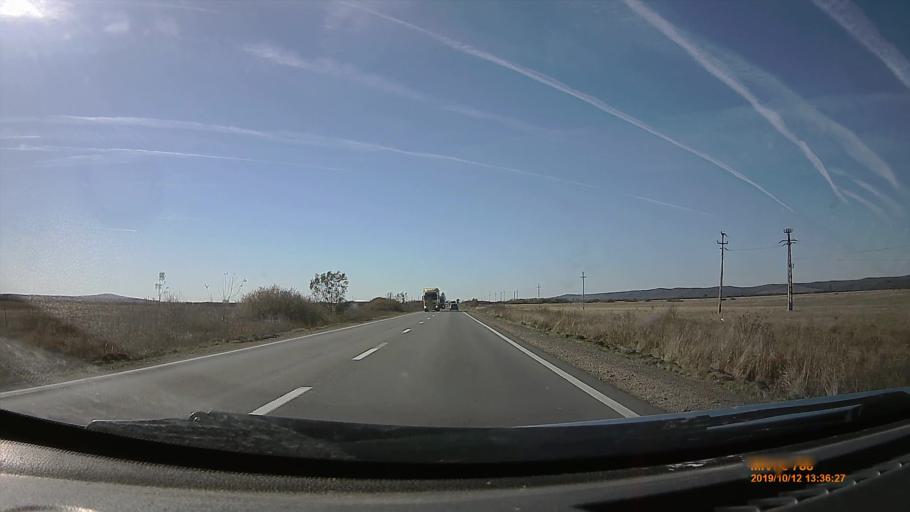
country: RO
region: Bihor
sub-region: Comuna Sacadat
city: Sacadat
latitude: 47.0601
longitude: 22.1372
